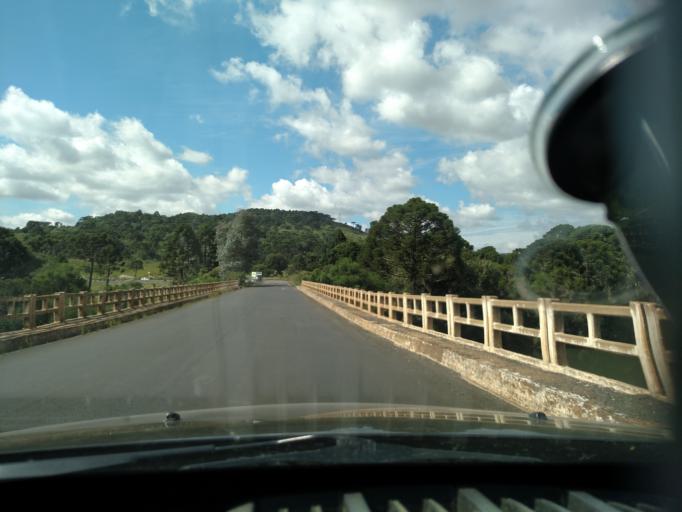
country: BR
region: Santa Catarina
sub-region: Sao Joaquim
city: Sao Joaquim
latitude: -28.0897
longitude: -50.0613
